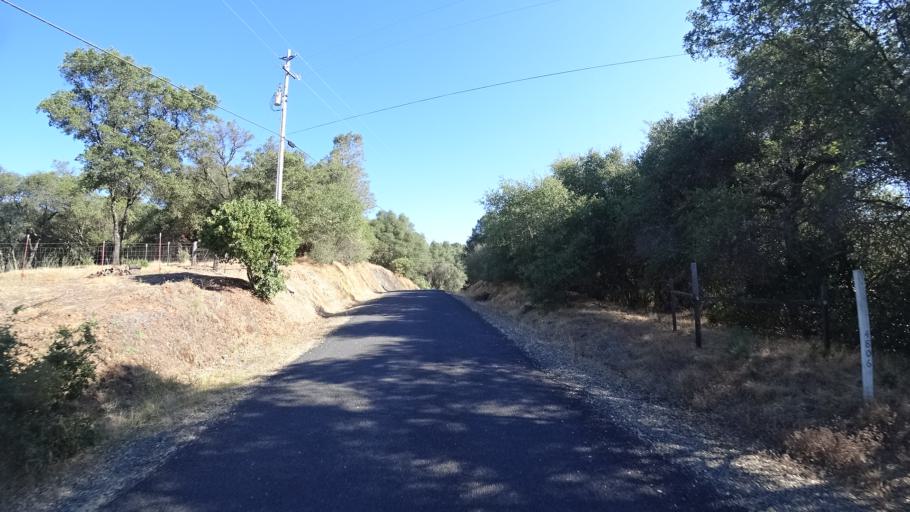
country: US
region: California
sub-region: Calaveras County
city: San Andreas
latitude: 38.2529
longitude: -120.7060
